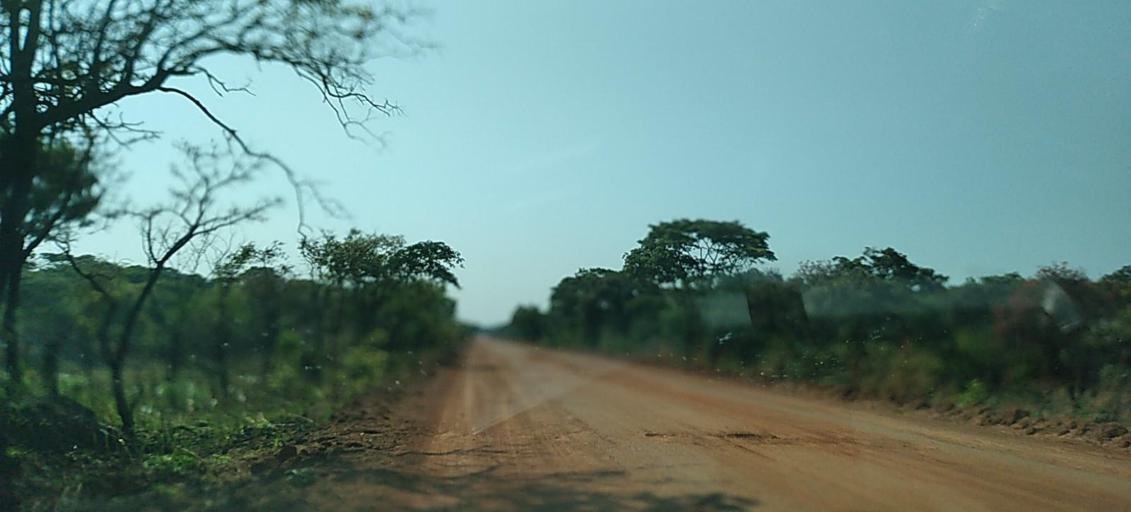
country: ZM
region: North-Western
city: Mwinilunga
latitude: -11.9160
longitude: 25.3080
